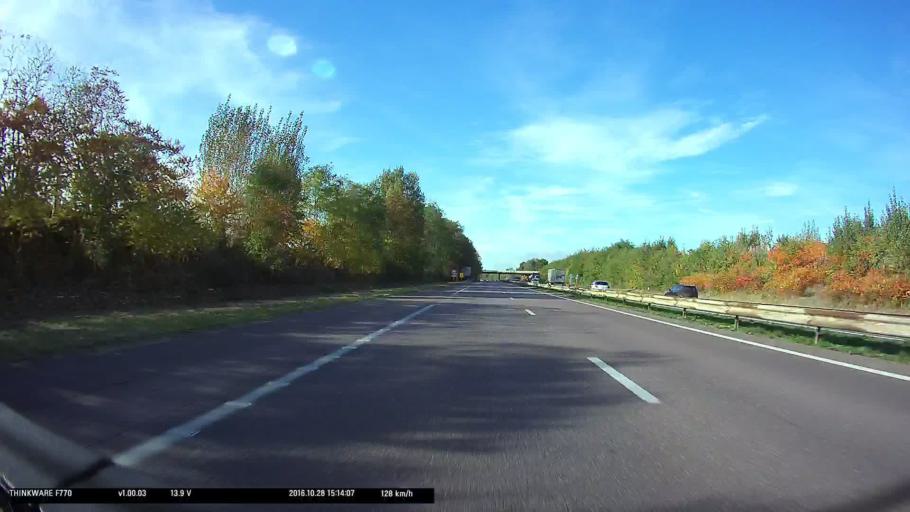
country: FR
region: Alsace
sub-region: Departement du Bas-Rhin
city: Mommenheim
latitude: 48.7575
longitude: 7.6705
